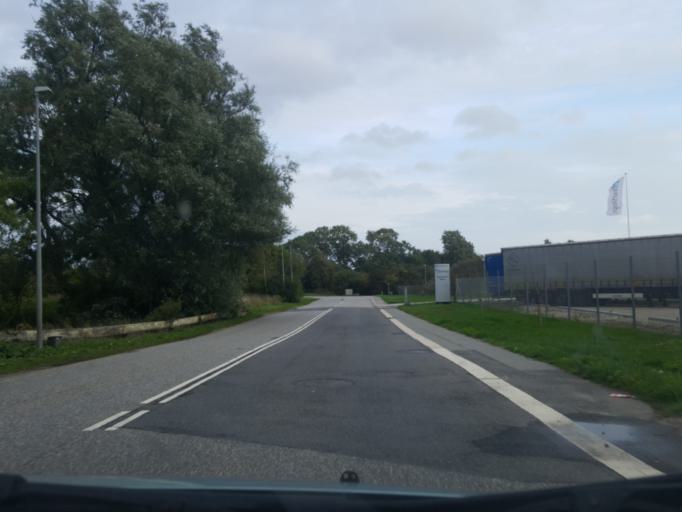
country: DK
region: South Denmark
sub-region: Fredericia Kommune
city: Taulov
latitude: 55.5419
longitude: 9.6334
